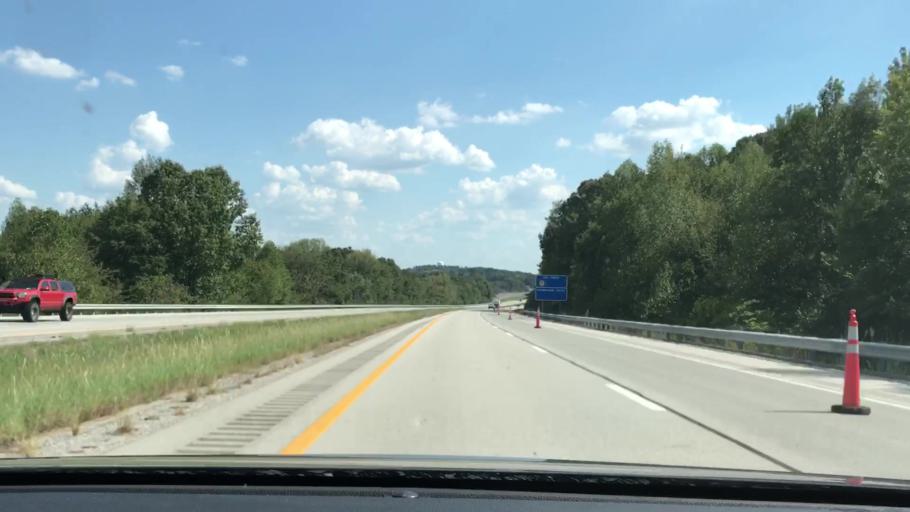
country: US
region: Kentucky
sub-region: Butler County
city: Morgantown
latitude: 37.2231
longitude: -86.7179
